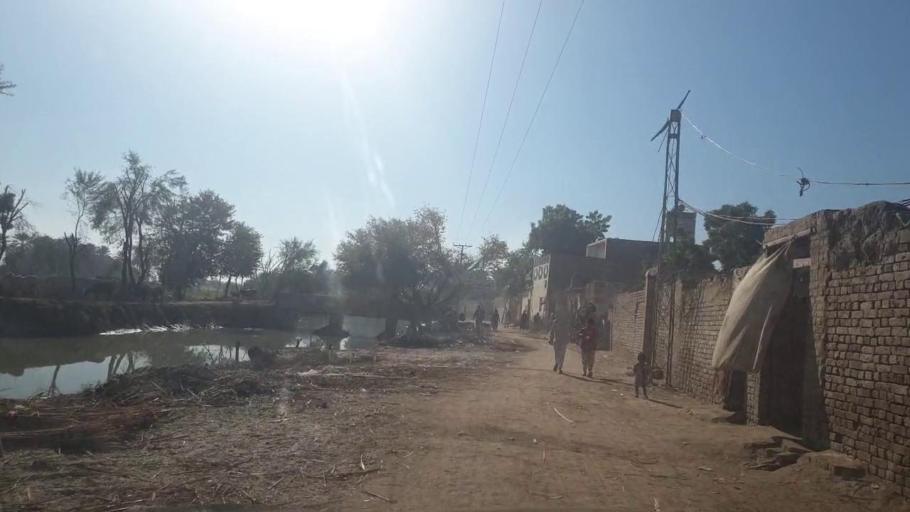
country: PK
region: Sindh
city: Ghotki
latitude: 27.9801
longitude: 69.3267
